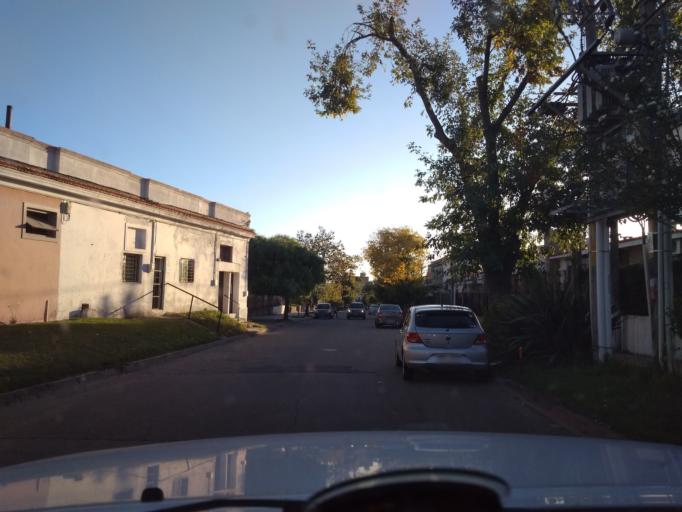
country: UY
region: Montevideo
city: Montevideo
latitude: -34.8913
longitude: -56.1402
